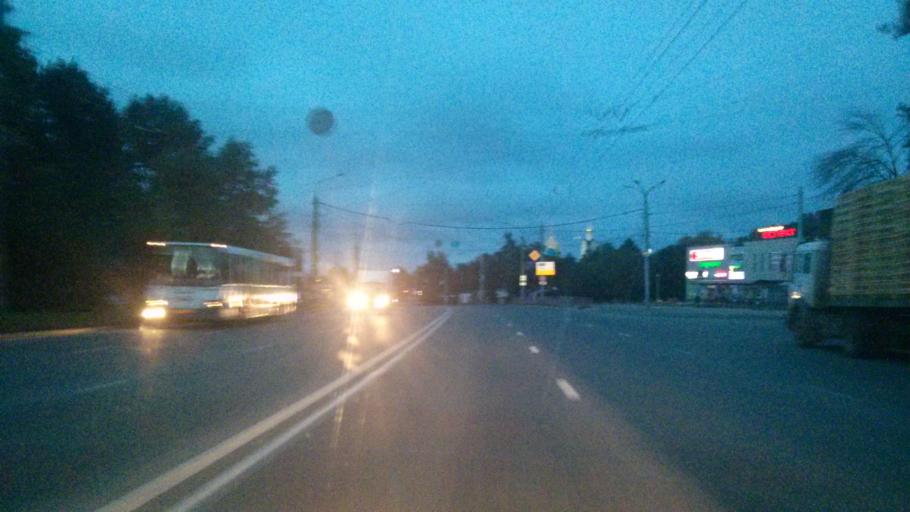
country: RU
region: Nizjnij Novgorod
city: Nizhniy Novgorod
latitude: 56.2318
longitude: 43.9473
